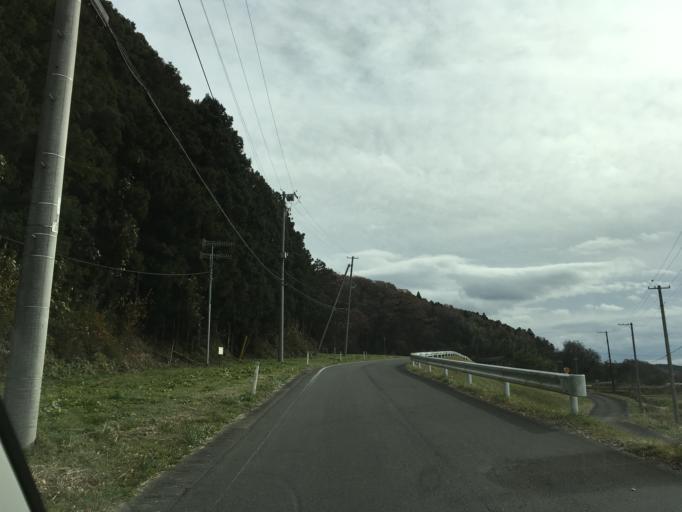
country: JP
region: Iwate
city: Ichinoseki
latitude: 38.7678
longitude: 141.2730
